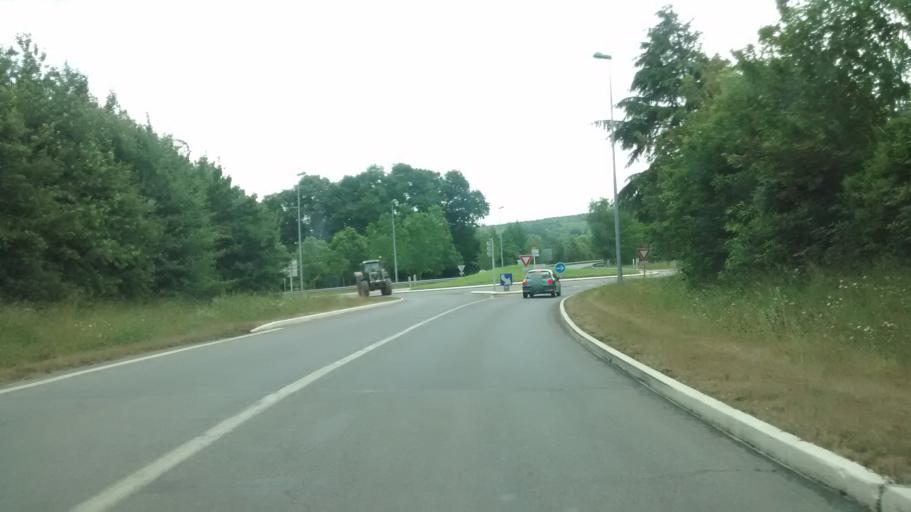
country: FR
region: Brittany
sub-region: Departement du Morbihan
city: La Gacilly
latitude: 47.7739
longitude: -2.1238
